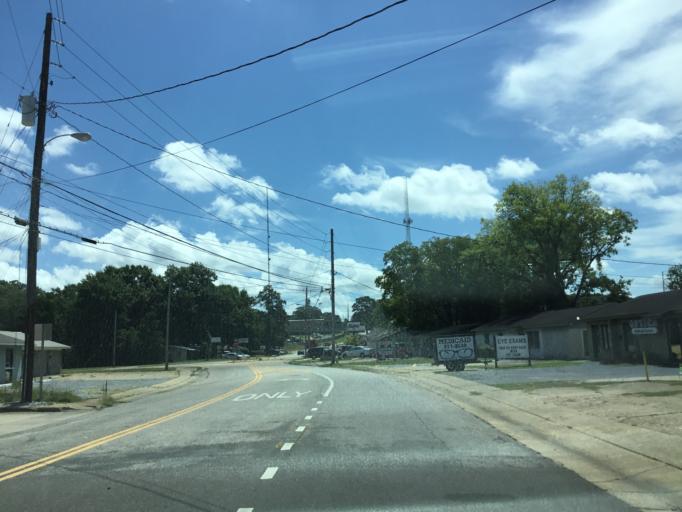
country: US
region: Alabama
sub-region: Montgomery County
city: Montgomery
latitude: 32.3673
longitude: -86.2709
